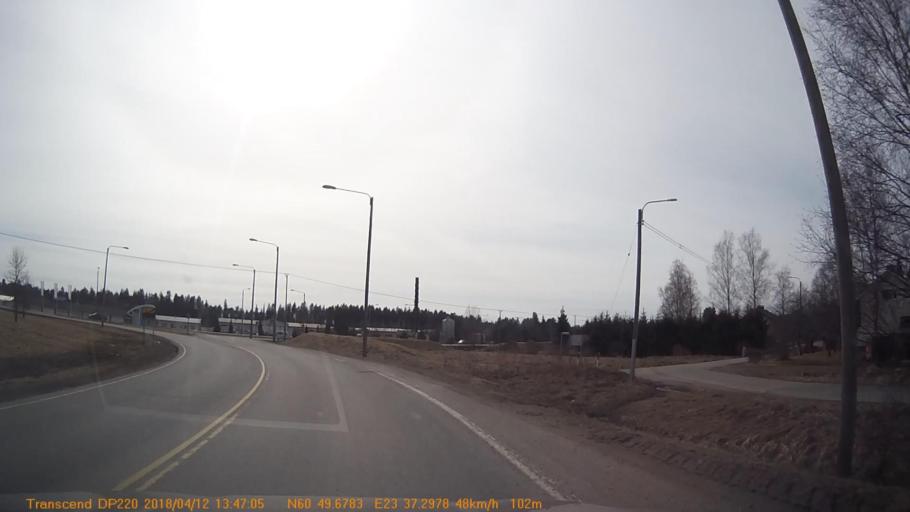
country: FI
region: Haeme
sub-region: Forssa
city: Forssa
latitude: 60.8279
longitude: 23.6219
